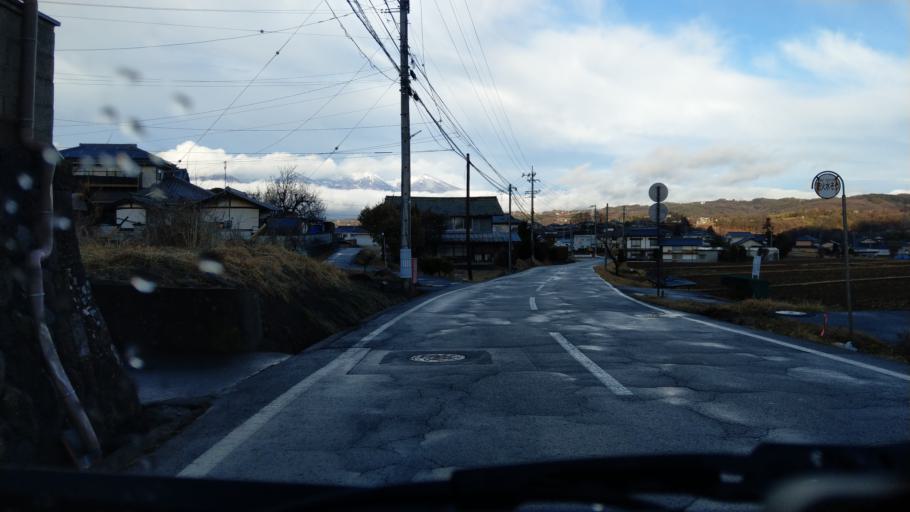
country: JP
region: Nagano
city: Kamimaruko
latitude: 36.2818
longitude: 138.3264
